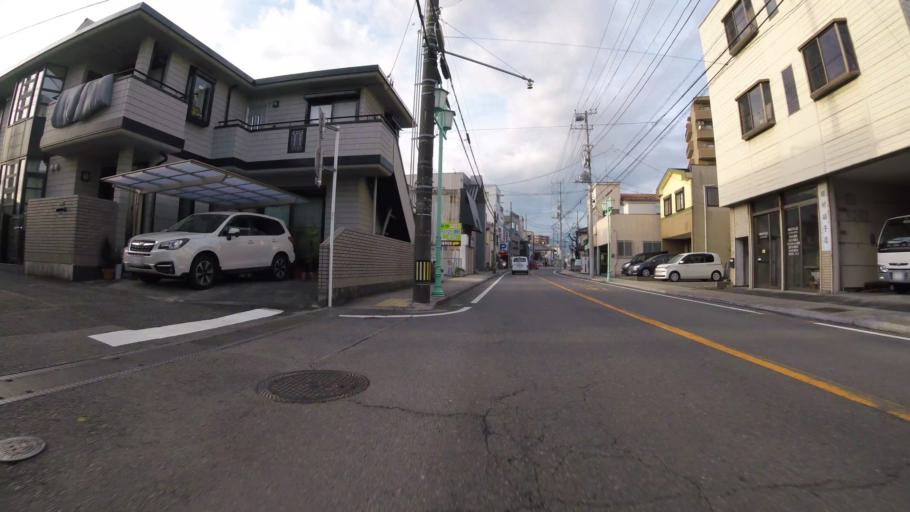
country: JP
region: Shizuoka
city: Mishima
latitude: 35.1159
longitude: 138.9218
